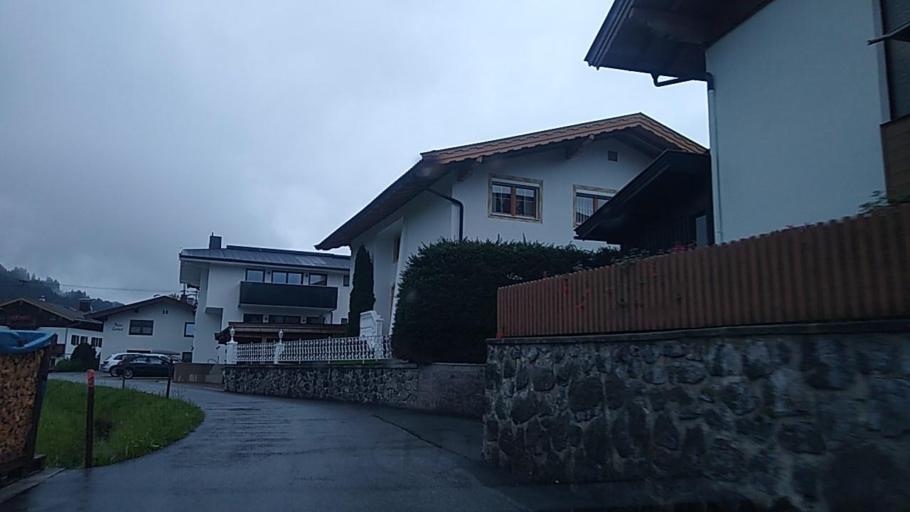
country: AT
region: Tyrol
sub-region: Politischer Bezirk Kitzbuhel
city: Brixen im Thale
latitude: 47.4462
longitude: 12.2394
